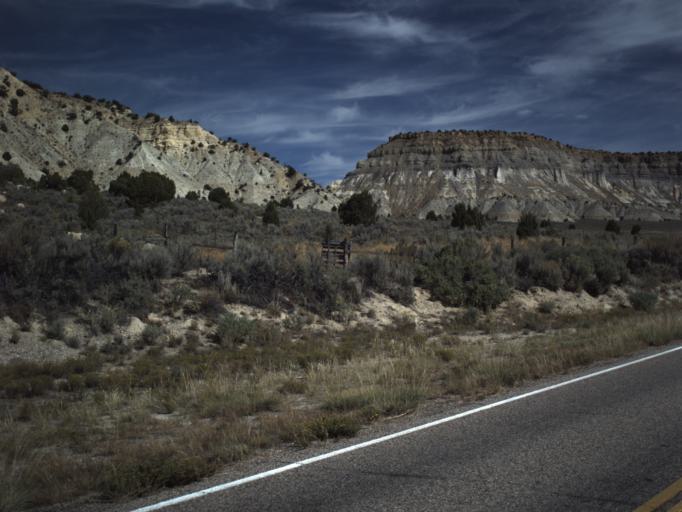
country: US
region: Utah
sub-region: Garfield County
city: Panguitch
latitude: 37.5598
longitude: -112.0166
